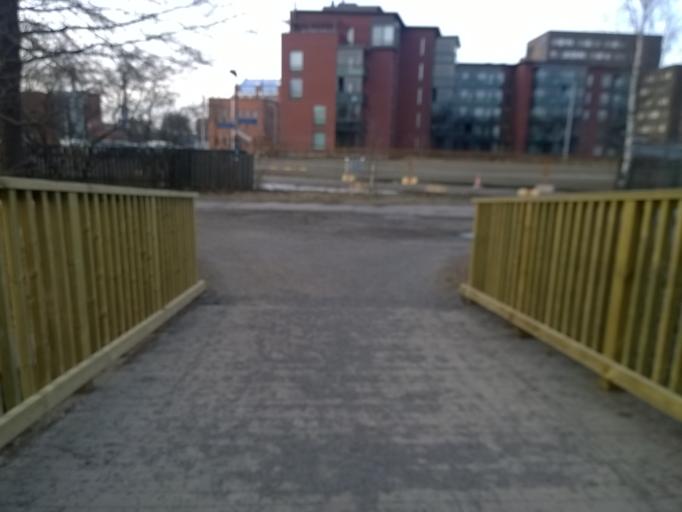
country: FI
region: Pirkanmaa
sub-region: Tampere
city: Tampere
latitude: 61.4899
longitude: 23.7690
